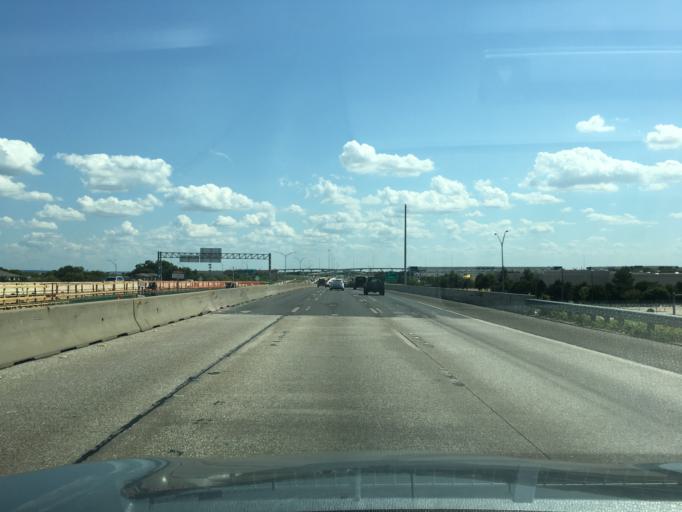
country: US
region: Texas
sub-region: Tarrant County
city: Arlington
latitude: 32.6925
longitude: -97.0627
